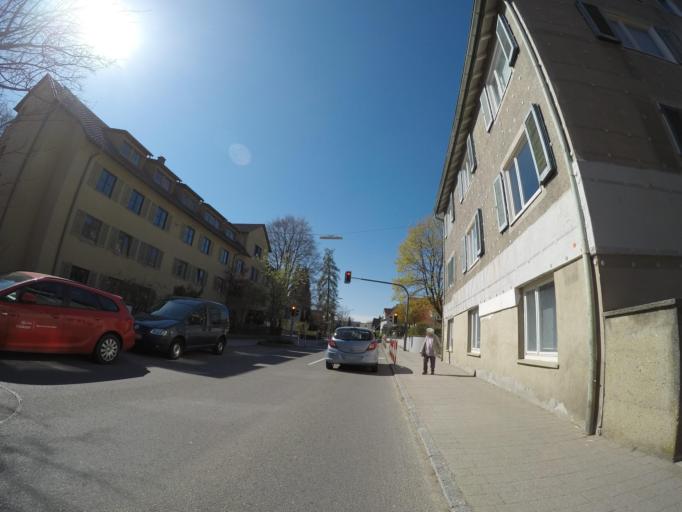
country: DE
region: Baden-Wuerttemberg
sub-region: Tuebingen Region
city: Wilhelmsdorf
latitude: 47.8650
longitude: 9.4242
